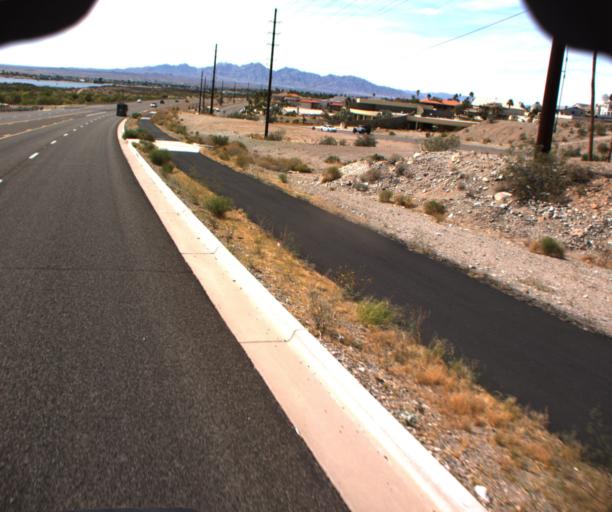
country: US
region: Arizona
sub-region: Mohave County
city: Lake Havasu City
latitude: 34.4529
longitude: -114.3214
